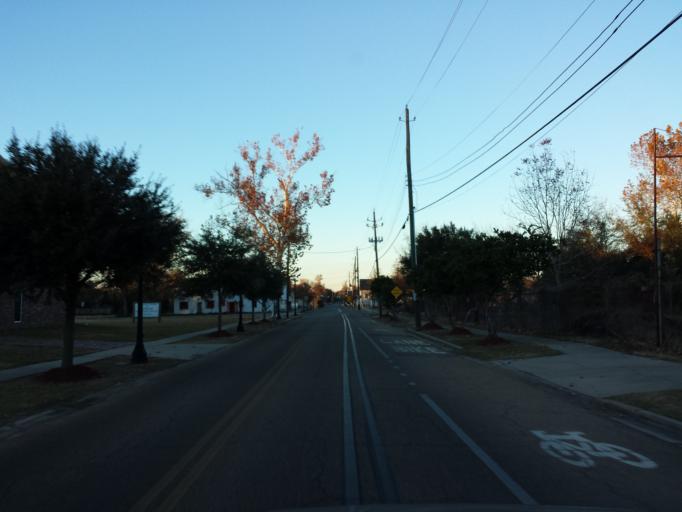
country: US
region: Mississippi
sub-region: Forrest County
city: Hattiesburg
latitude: 31.3312
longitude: -89.2900
